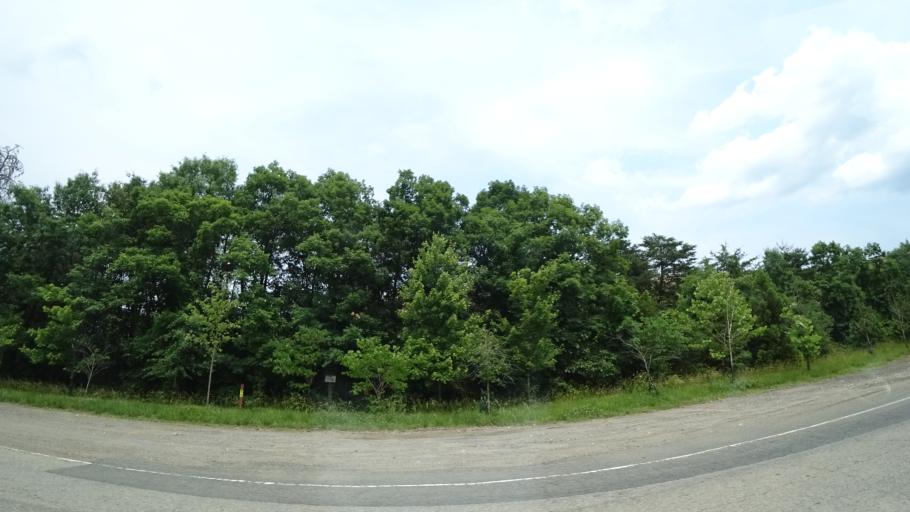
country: US
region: Virginia
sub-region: Fairfax County
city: Lorton
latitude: 38.6847
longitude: -77.2371
